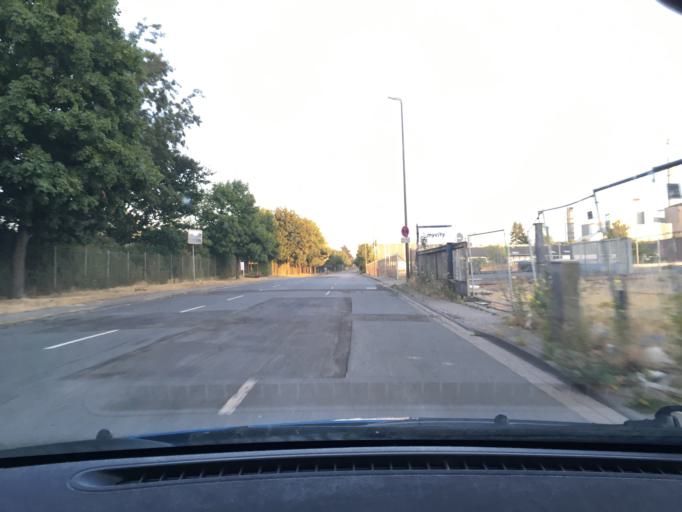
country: DE
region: Lower Saxony
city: Uelzen
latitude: 52.9834
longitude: 10.5590
